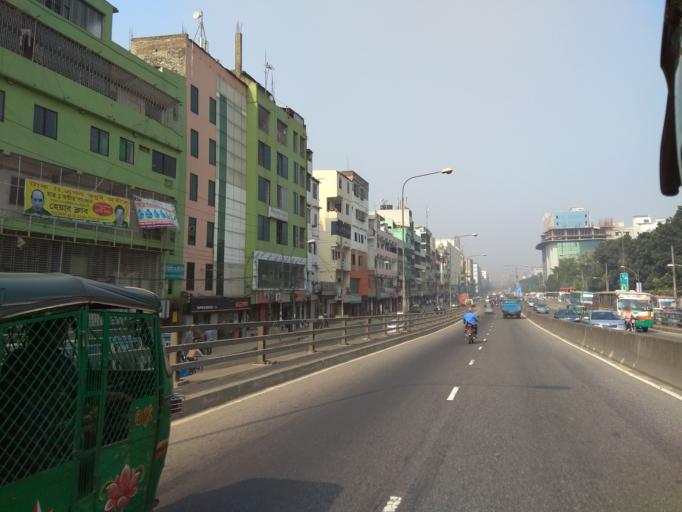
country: BD
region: Dhaka
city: Paltan
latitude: 23.7825
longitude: 90.3989
